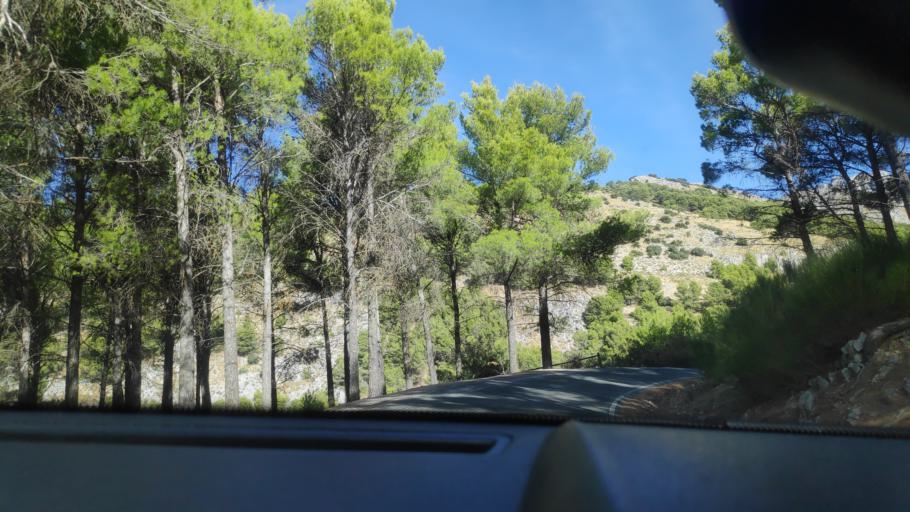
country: ES
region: Andalusia
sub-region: Provincia de Jaen
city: Torres
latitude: 37.7834
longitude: -3.4946
